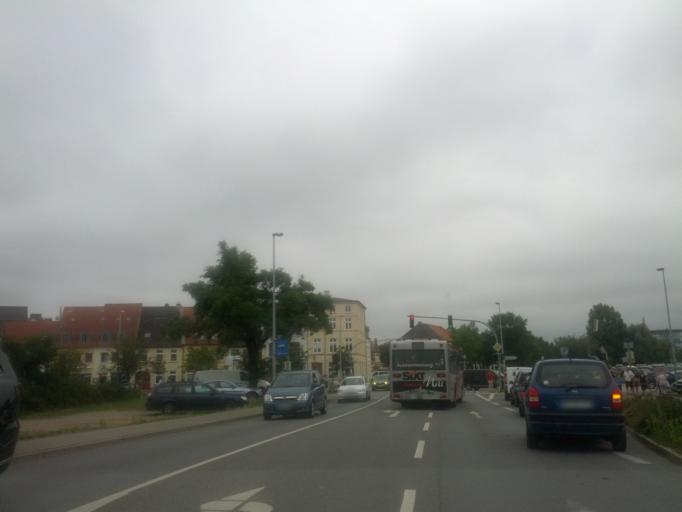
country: DE
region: Mecklenburg-Vorpommern
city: Wismar
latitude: 53.8953
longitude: 11.4605
